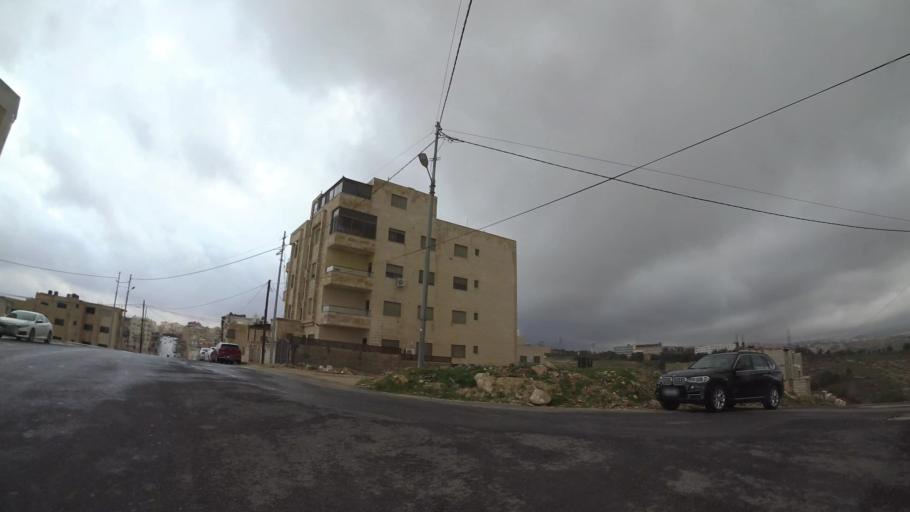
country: JO
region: Amman
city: Amman
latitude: 32.0071
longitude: 35.9303
